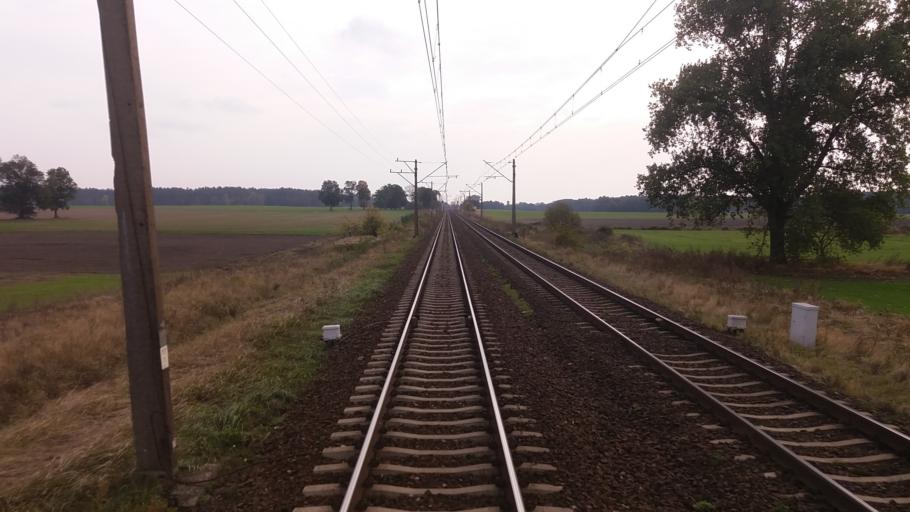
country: PL
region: West Pomeranian Voivodeship
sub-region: Powiat stargardzki
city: Dolice
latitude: 53.2173
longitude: 15.1573
